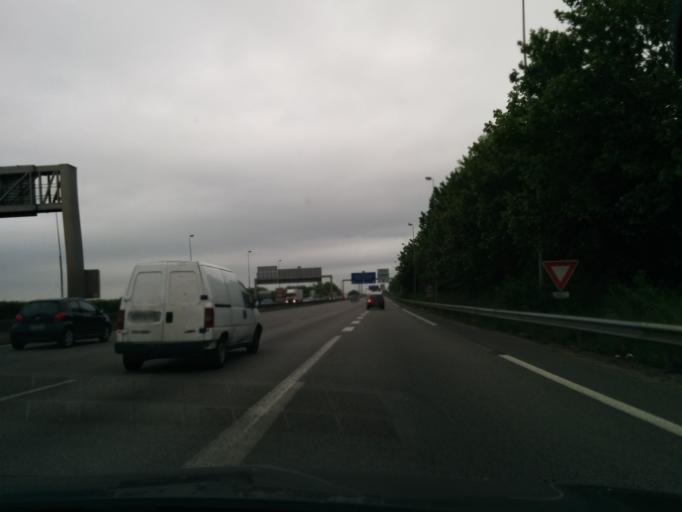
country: FR
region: Ile-de-France
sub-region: Departement des Yvelines
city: Buchelay
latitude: 48.9824
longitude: 1.6854
